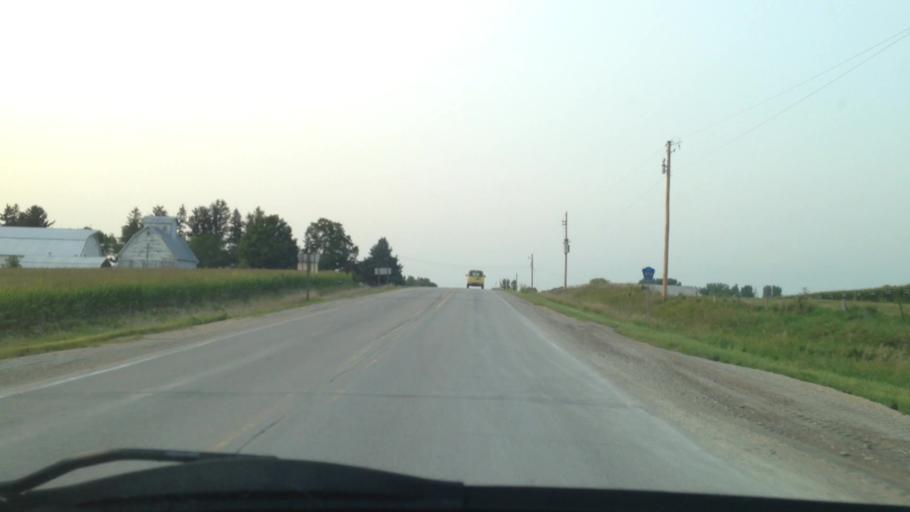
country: US
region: Iowa
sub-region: Benton County
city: Atkins
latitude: 41.9927
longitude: -91.8732
